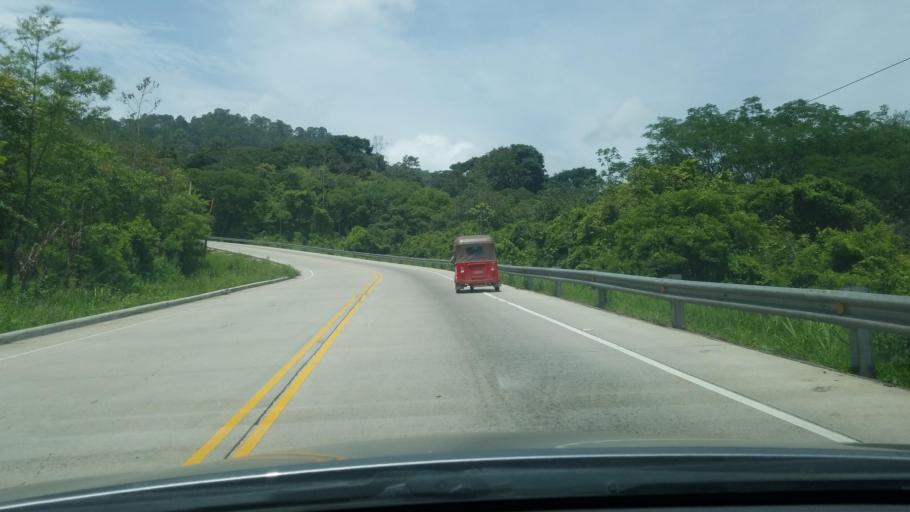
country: HN
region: Copan
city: Agua Caliente
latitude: 14.8786
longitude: -88.7802
